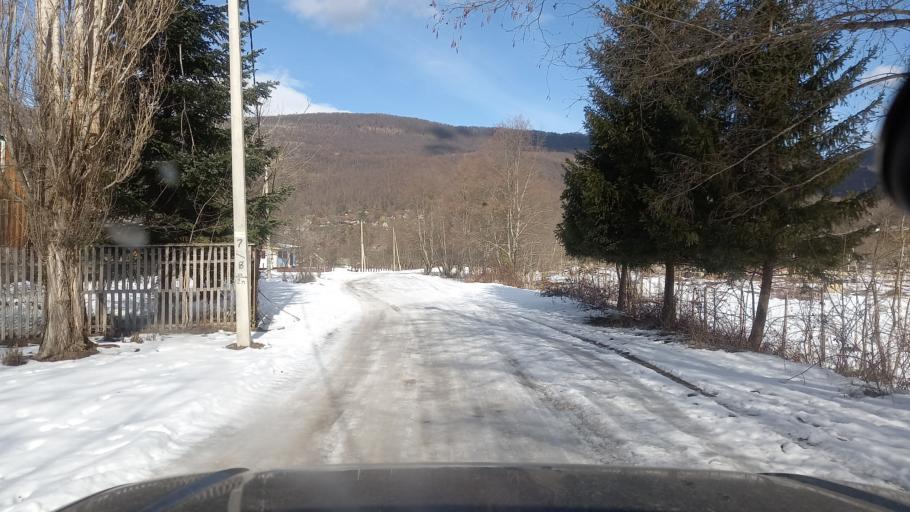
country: RU
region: Adygeya
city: Kamennomostskiy
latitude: 44.1934
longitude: 39.9608
